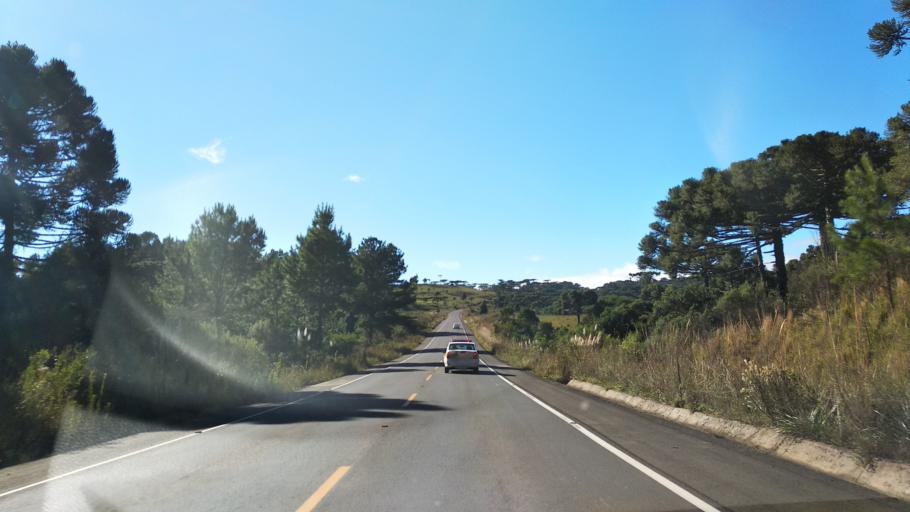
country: BR
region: Santa Catarina
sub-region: Lages
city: Lages
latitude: -27.8932
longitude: -50.1383
